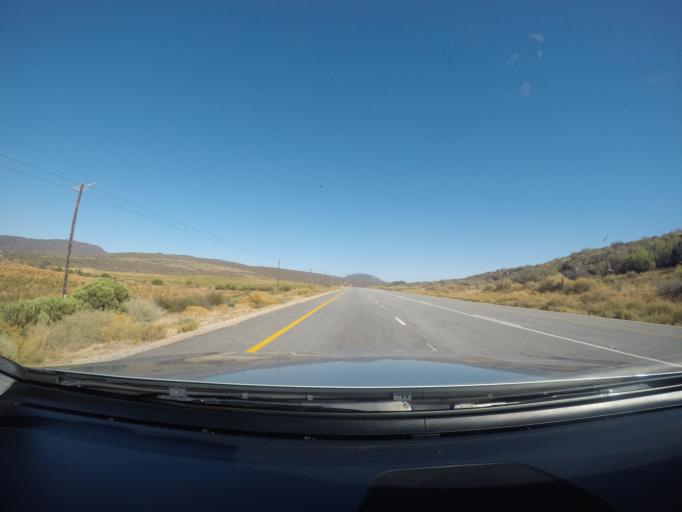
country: ZA
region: Western Cape
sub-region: West Coast District Municipality
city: Clanwilliam
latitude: -32.3223
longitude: 18.9162
